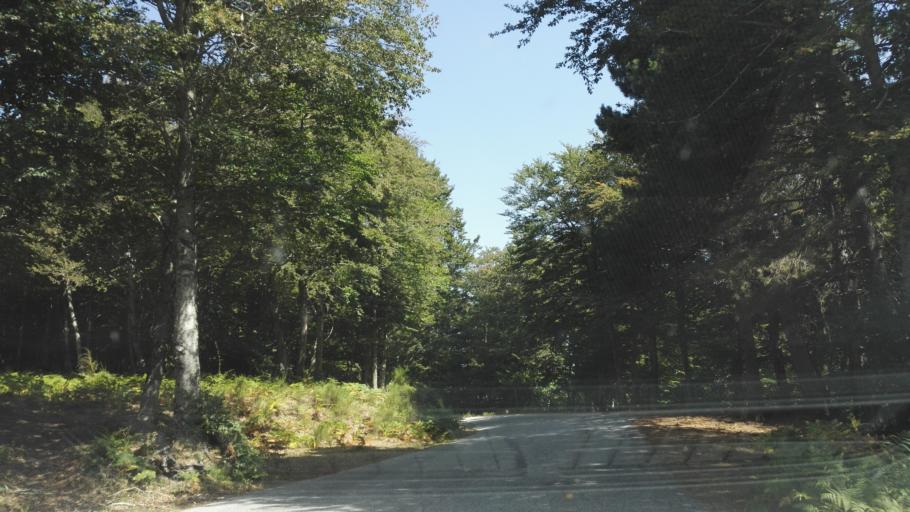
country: IT
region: Calabria
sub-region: Provincia di Vibo-Valentia
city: Nardodipace
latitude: 38.4885
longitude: 16.3689
